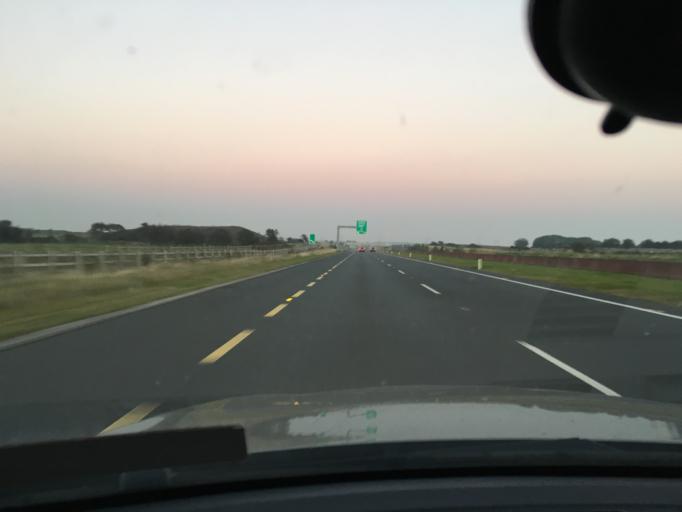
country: IE
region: Connaught
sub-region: County Galway
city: Oranmore
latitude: 53.2952
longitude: -8.9350
